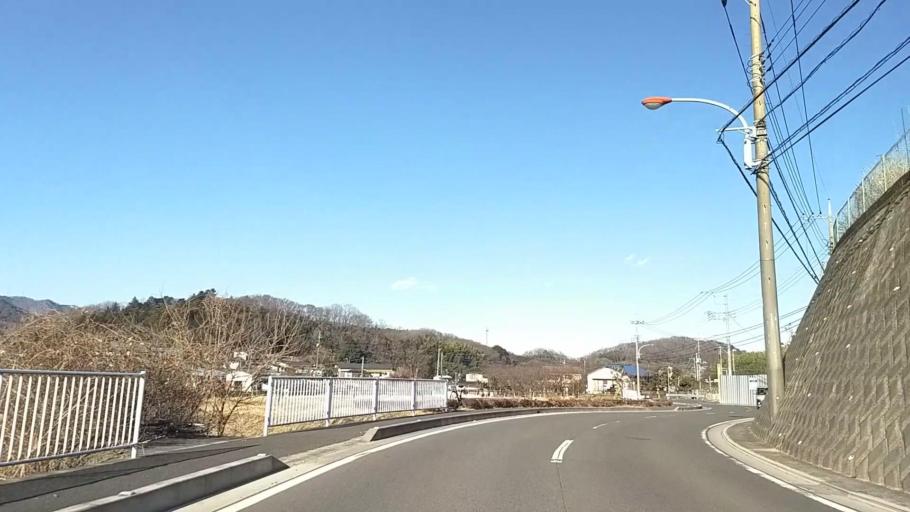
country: JP
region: Kanagawa
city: Atsugi
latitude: 35.4568
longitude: 139.3124
